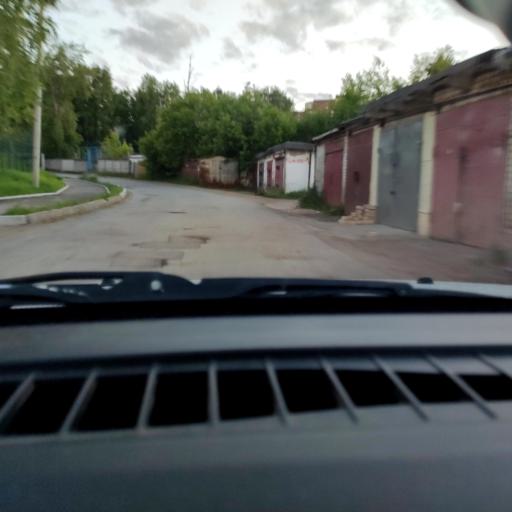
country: RU
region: Perm
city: Perm
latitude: 58.1156
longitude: 56.3104
